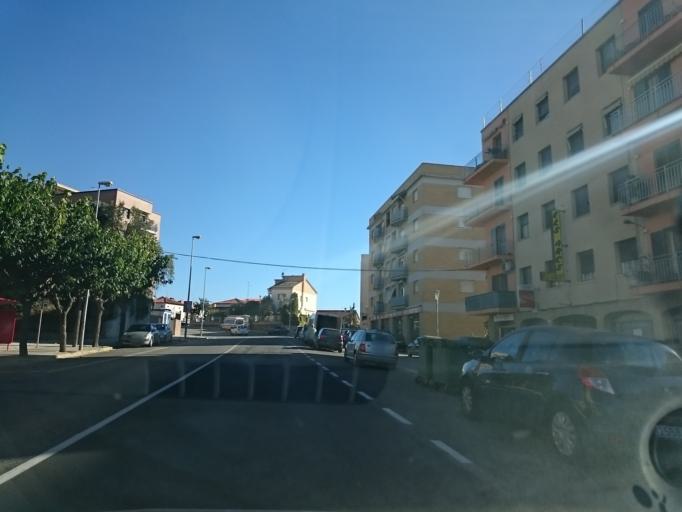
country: ES
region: Catalonia
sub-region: Provincia de Barcelona
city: Piera
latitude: 41.5249
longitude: 1.7500
